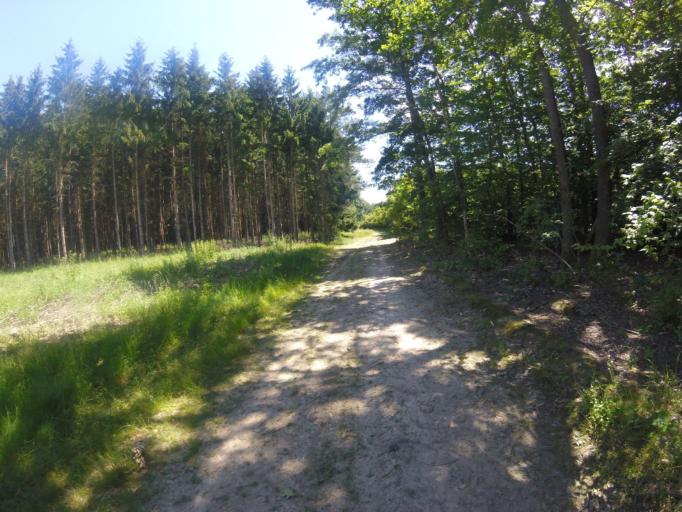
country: HU
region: Zala
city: Zalalovo
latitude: 46.8247
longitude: 16.5146
